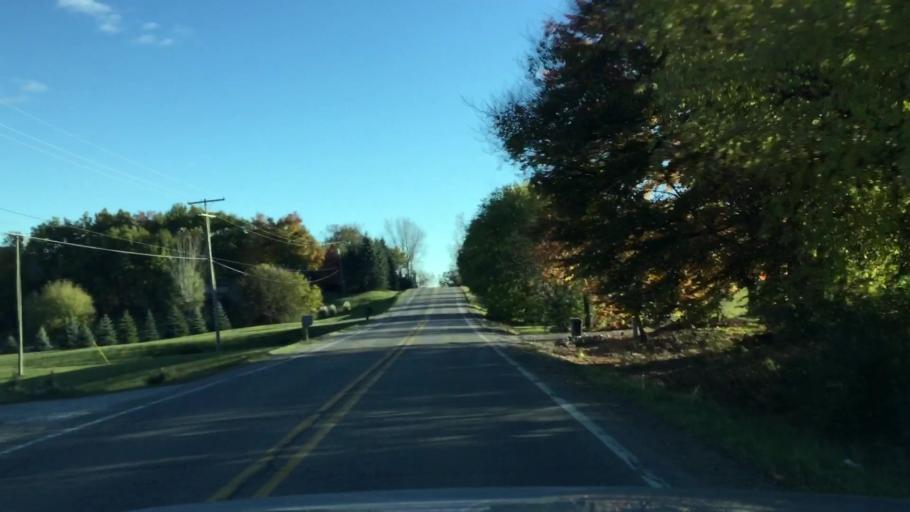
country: US
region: Michigan
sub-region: Lapeer County
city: Imlay City
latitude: 43.0435
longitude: -83.1673
